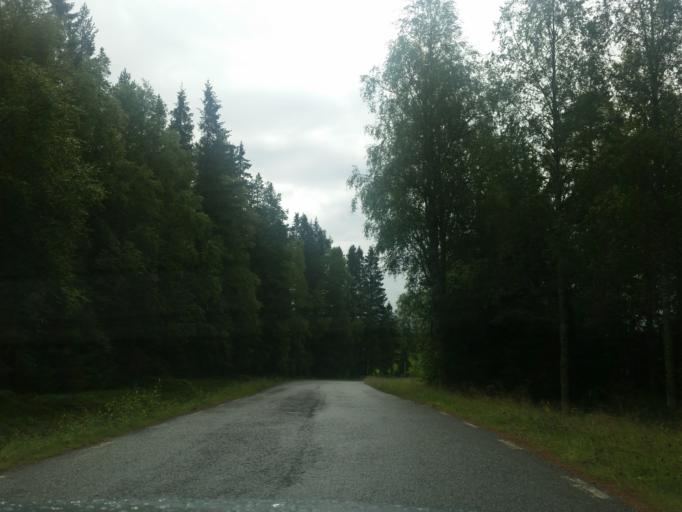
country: SE
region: Vaesterbotten
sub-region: Robertsfors Kommun
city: Robertsfors
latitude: 64.0333
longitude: 20.8440
